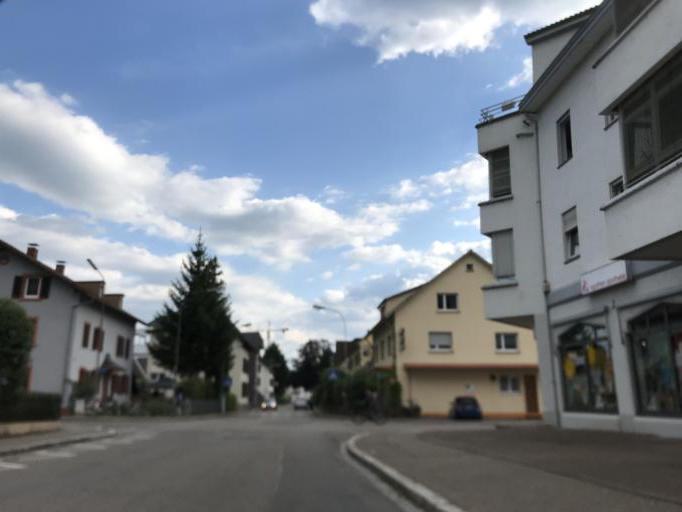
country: DE
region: Baden-Wuerttemberg
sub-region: Freiburg Region
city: Schopfheim
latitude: 47.6587
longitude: 7.8362
